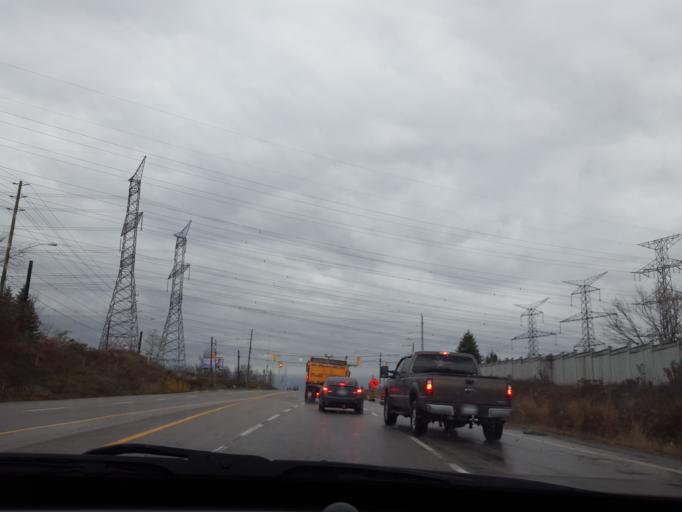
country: CA
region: Ontario
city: Ajax
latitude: 43.8664
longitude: -79.0824
